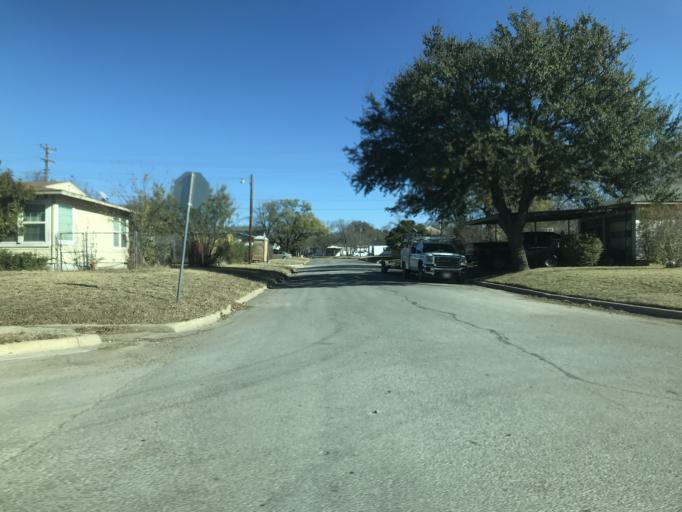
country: US
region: Texas
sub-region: Taylor County
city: Abilene
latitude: 32.4342
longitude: -99.7537
